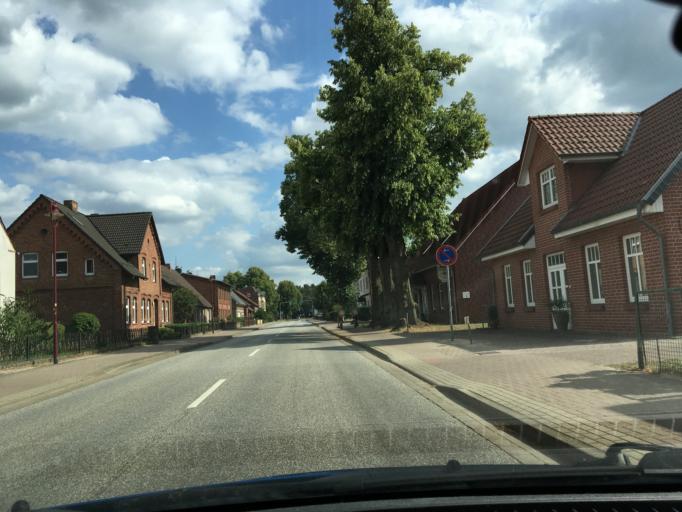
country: DE
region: Mecklenburg-Vorpommern
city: Lubtheen
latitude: 53.3001
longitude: 11.0832
